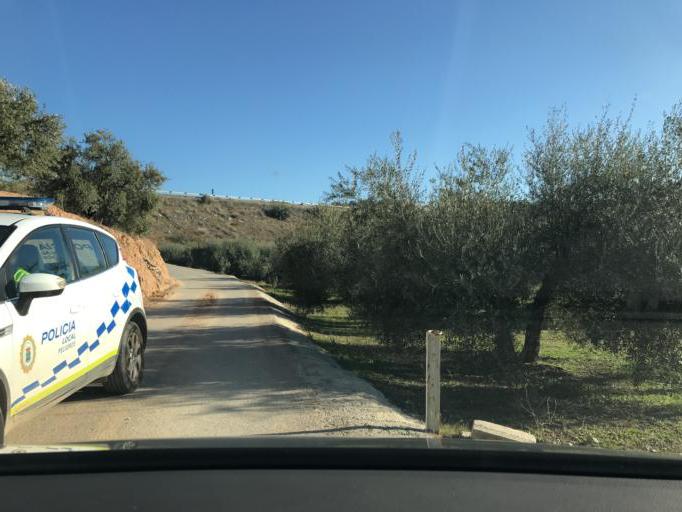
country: ES
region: Andalusia
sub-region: Provincia de Granada
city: Peligros
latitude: 37.2384
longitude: -3.6181
